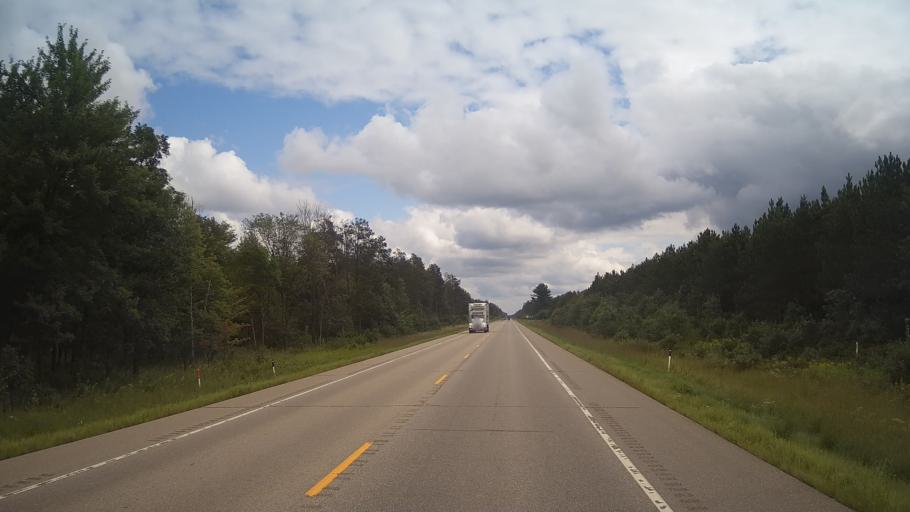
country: US
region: Wisconsin
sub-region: Adams County
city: Friendship
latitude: 44.0251
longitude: -89.7535
